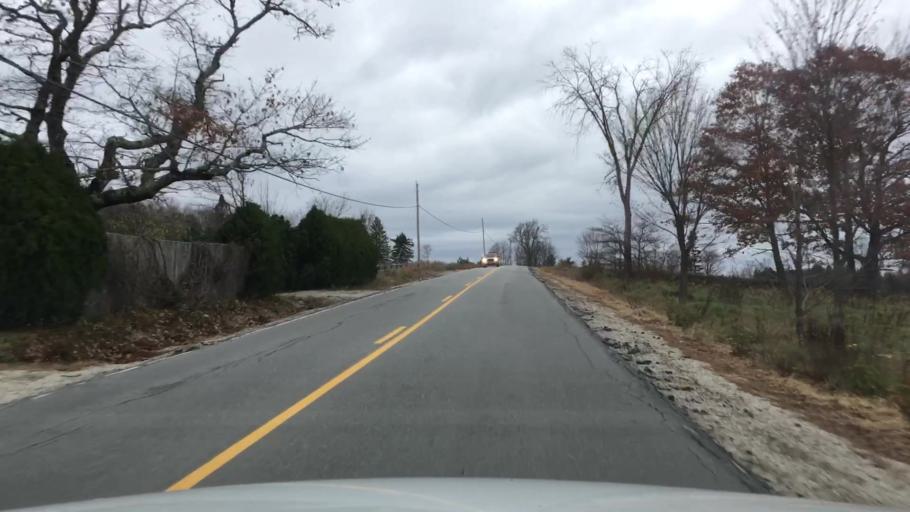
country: US
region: Maine
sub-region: Hancock County
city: Penobscot
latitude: 44.4393
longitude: -68.6345
